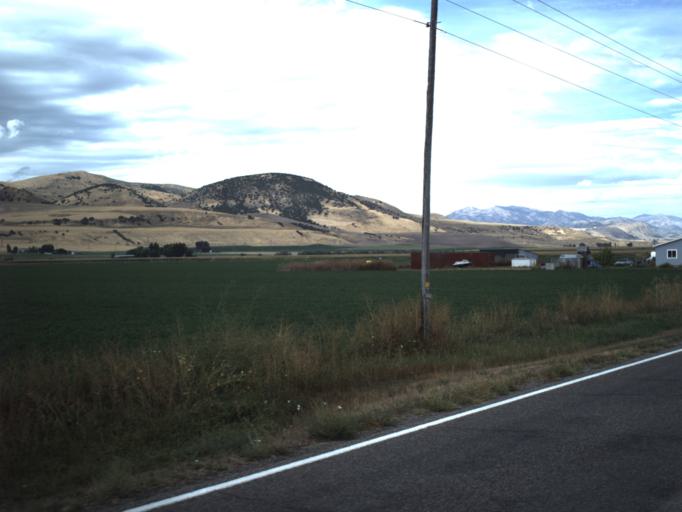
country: US
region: Utah
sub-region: Cache County
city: Lewiston
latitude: 41.9685
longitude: -111.9541
